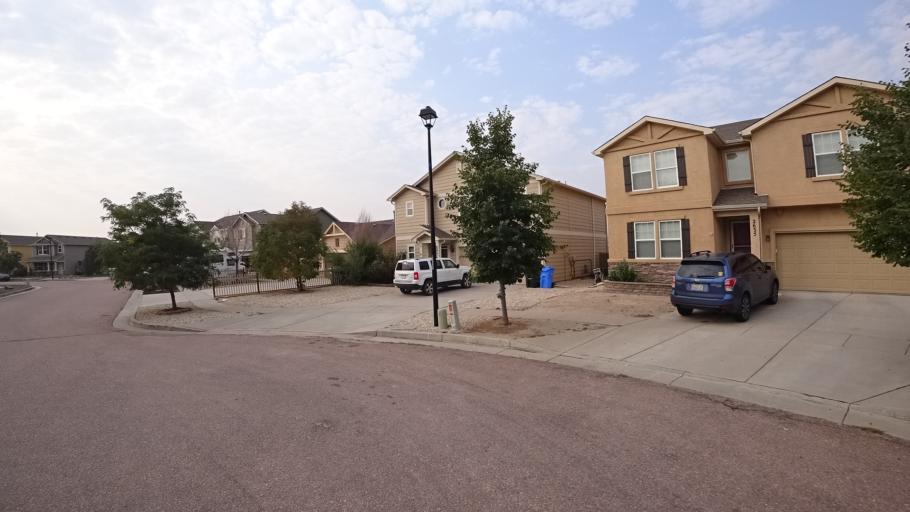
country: US
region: Colorado
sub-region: El Paso County
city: Stratmoor
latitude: 38.8006
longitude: -104.7792
